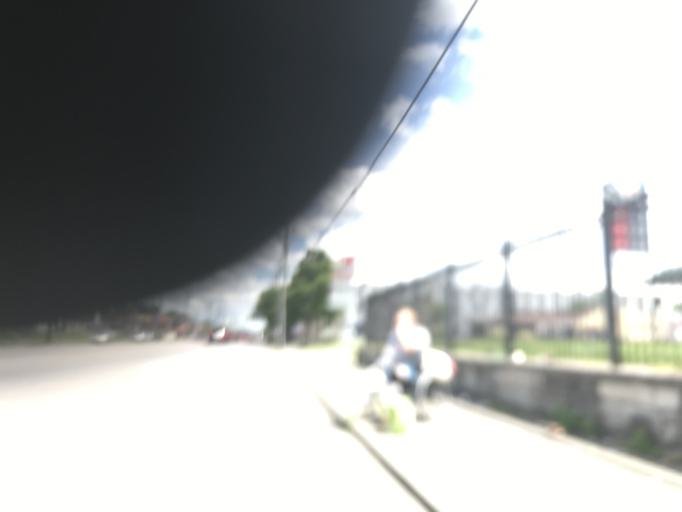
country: US
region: Kentucky
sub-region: Jefferson County
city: Louisville
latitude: 38.2494
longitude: -85.7967
